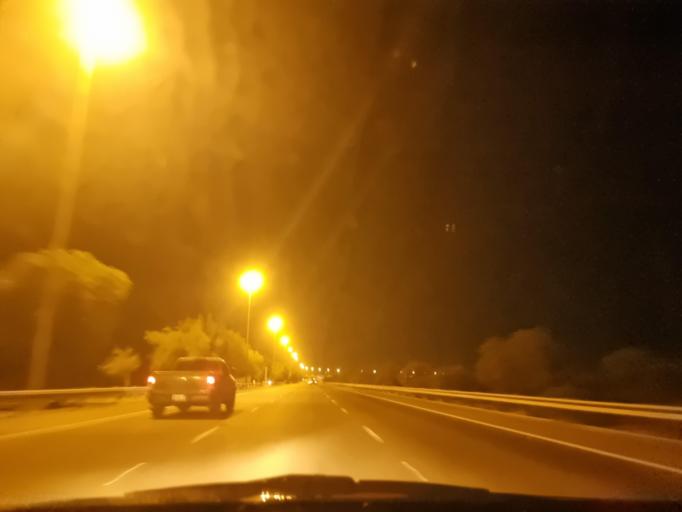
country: AE
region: Abu Dhabi
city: Al Ain
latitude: 24.1804
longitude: 55.0456
